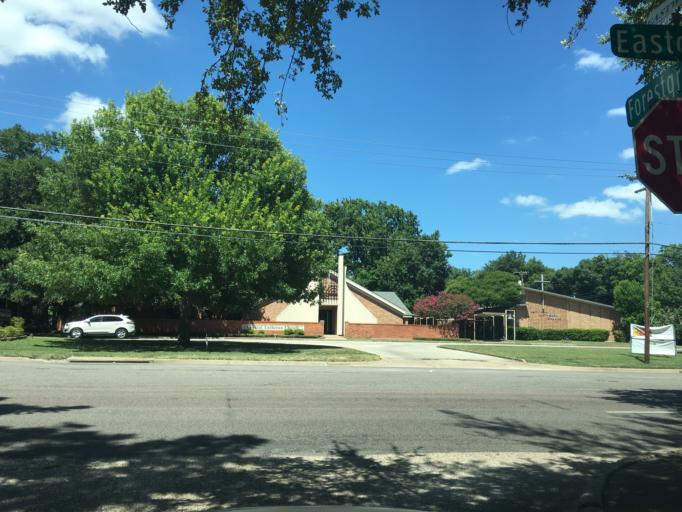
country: US
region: Texas
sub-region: Dallas County
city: Garland
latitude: 32.8464
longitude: -96.6951
